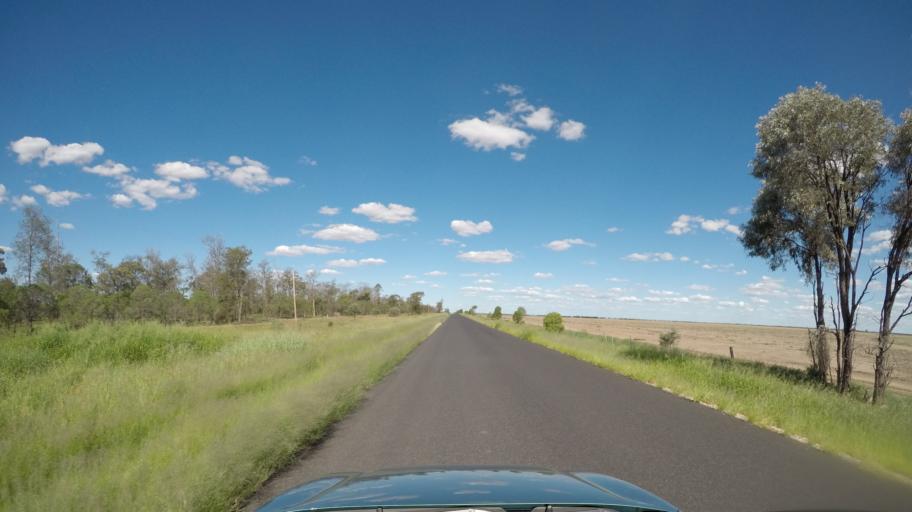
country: AU
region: Queensland
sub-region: Goondiwindi
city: Goondiwindi
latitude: -28.1626
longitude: 150.1505
